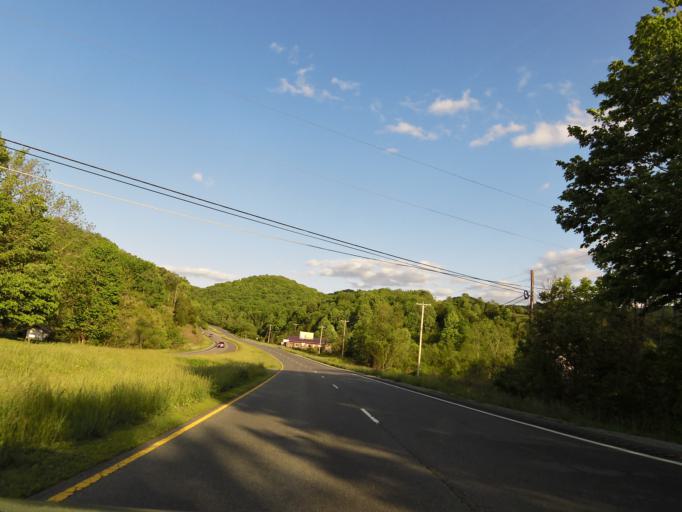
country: US
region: Virginia
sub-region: Russell County
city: Lebanon
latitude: 36.8156
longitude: -82.1273
